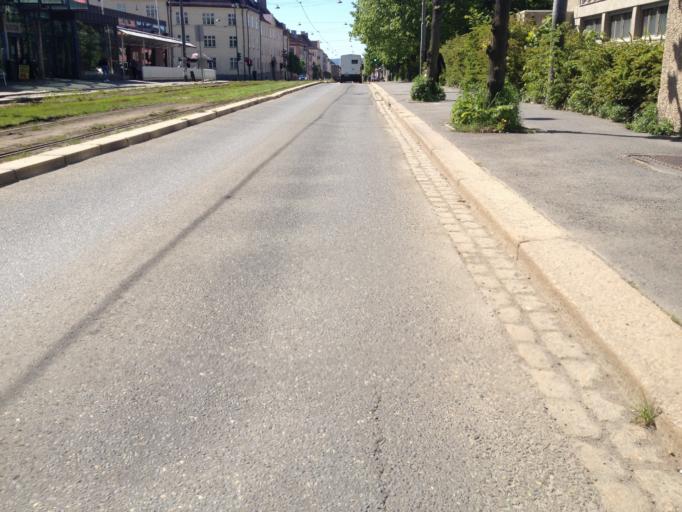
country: NO
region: Oslo
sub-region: Oslo
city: Oslo
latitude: 59.9381
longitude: 10.7678
